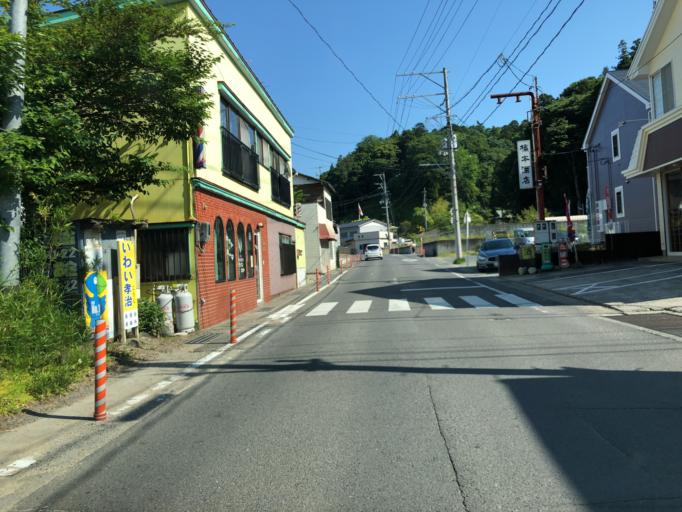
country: JP
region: Fukushima
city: Iwaki
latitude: 37.0008
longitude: 140.8517
